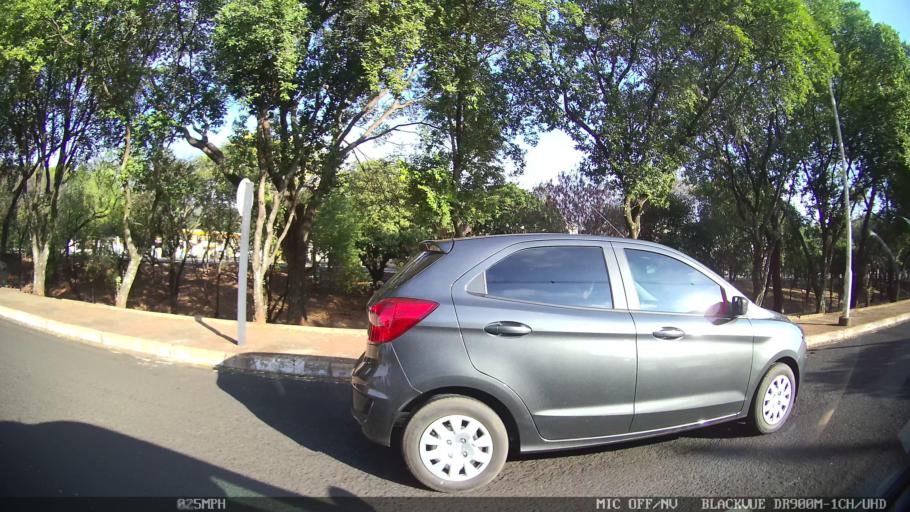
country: BR
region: Sao Paulo
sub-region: Sao Jose Do Rio Preto
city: Sao Jose do Rio Preto
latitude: -20.8243
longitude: -49.3657
